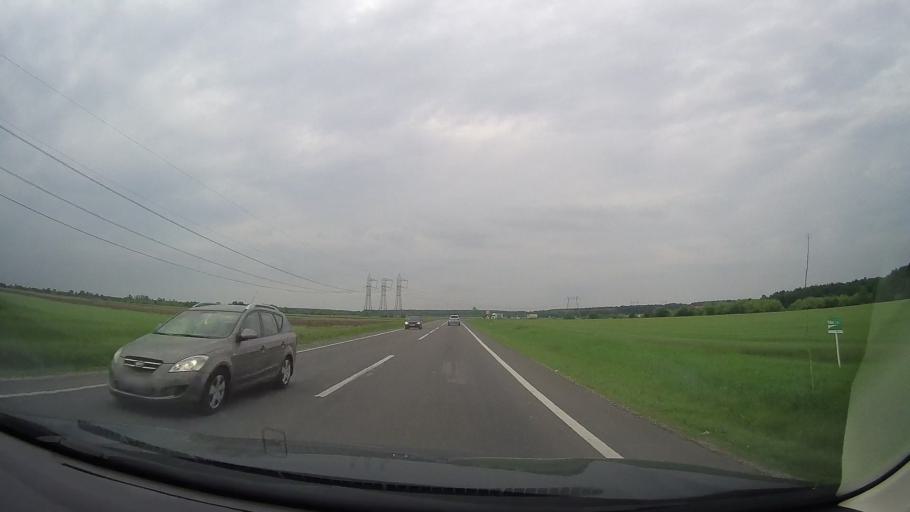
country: RO
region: Arges
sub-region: Comuna Sapata
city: Martesti
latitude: 44.7264
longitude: 24.7959
